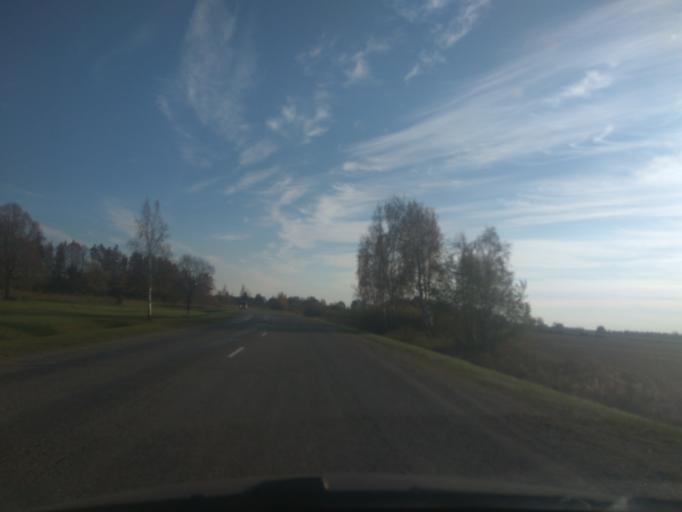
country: LV
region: Ventspils
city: Ventspils
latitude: 57.3489
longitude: 21.5655
